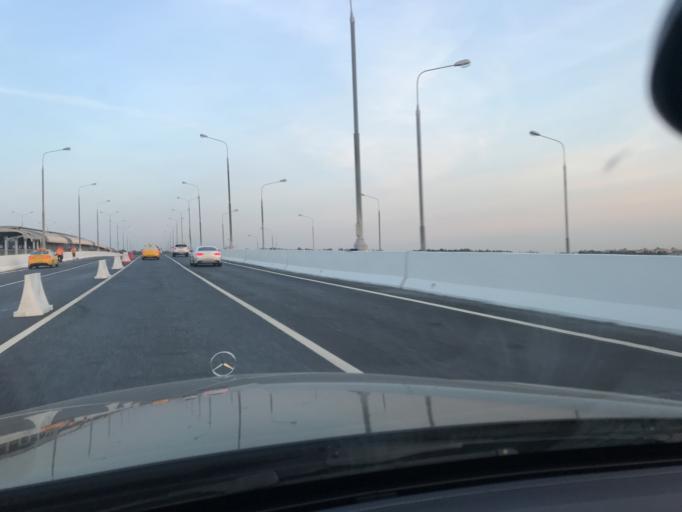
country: RU
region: Moskovskaya
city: Mosrentgen
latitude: 55.5853
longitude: 37.4355
